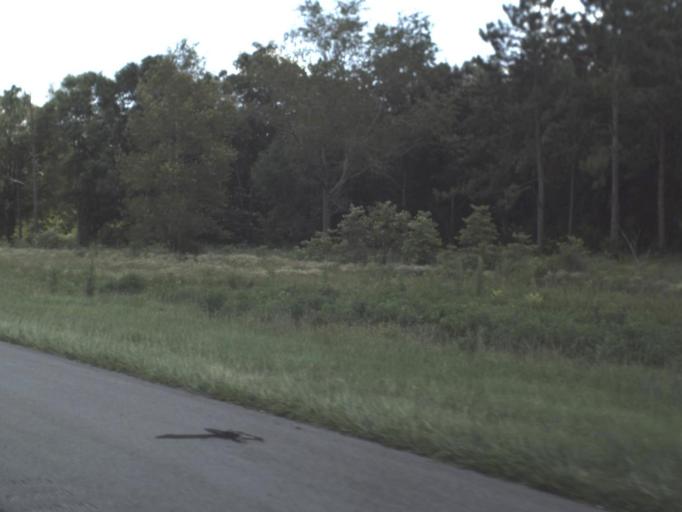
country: US
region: Florida
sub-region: Madison County
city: Madison
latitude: 30.3854
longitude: -83.3172
